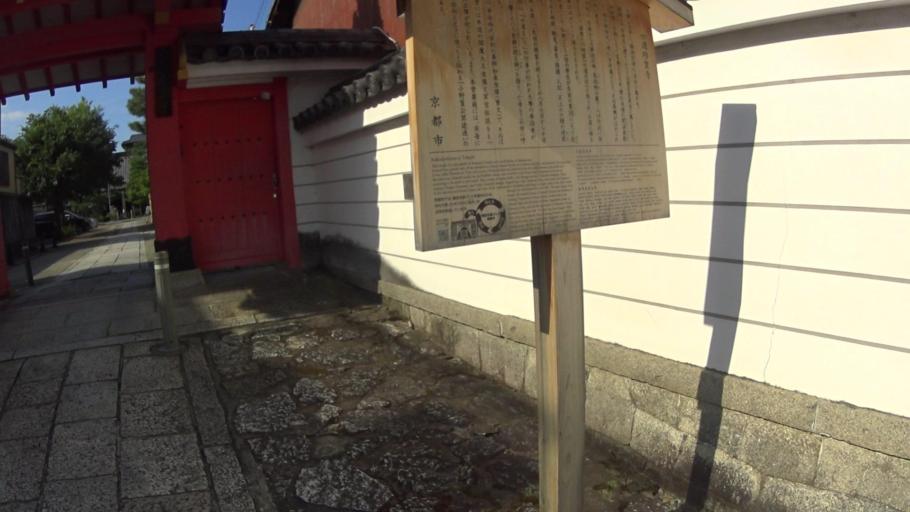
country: RU
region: Rostov
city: Remontnoye
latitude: 46.4994
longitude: 43.7743
